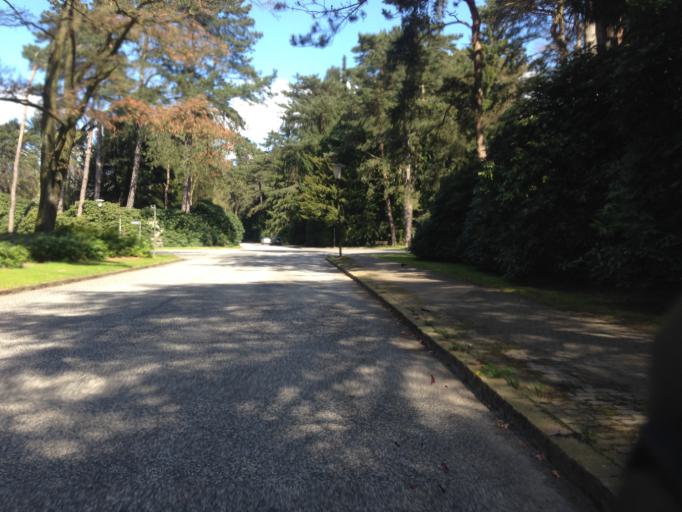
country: DE
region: Hamburg
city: Steilshoop
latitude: 53.6193
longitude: 10.0479
